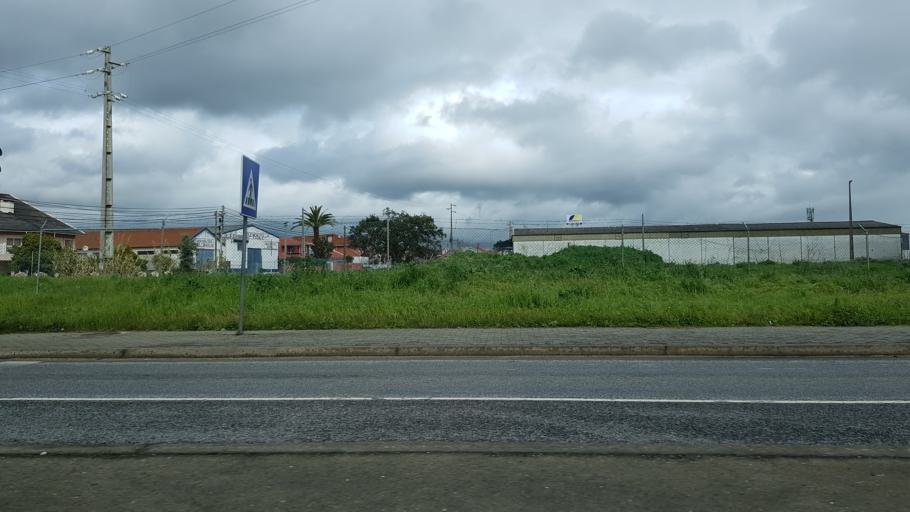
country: PT
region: Lisbon
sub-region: Alenquer
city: Carregado
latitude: 39.0393
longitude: -8.9859
